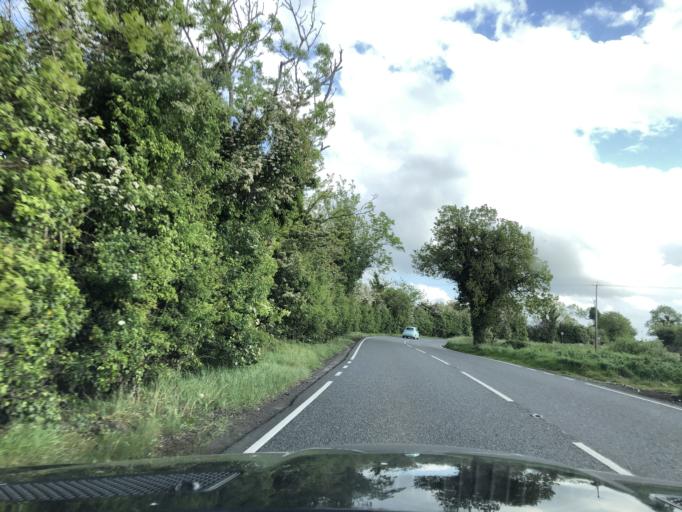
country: GB
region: Northern Ireland
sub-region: Antrim Borough
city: Antrim
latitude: 54.6682
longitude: -6.2193
